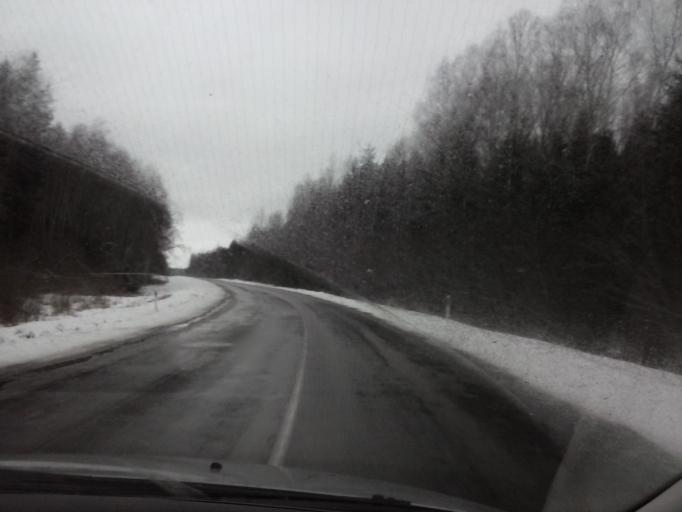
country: LV
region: Valkas Rajons
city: Valka
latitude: 57.7159
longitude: 25.9324
